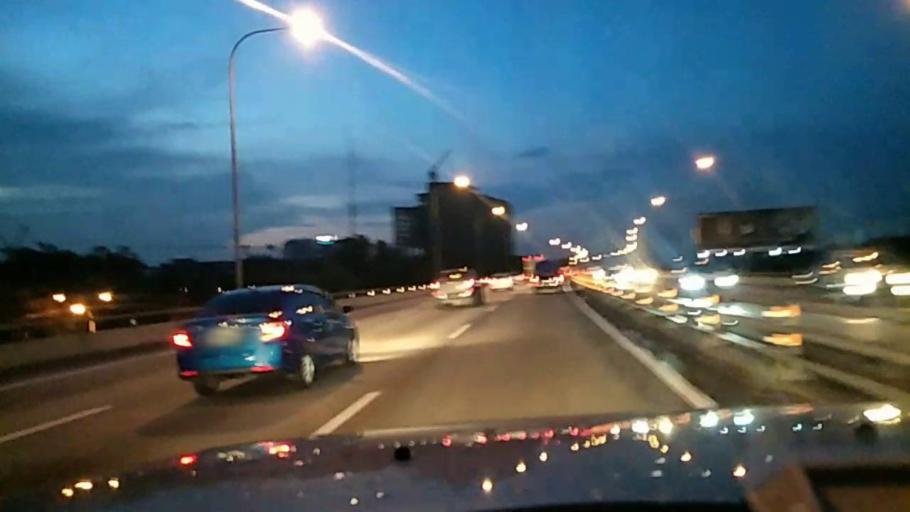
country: MY
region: Selangor
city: Shah Alam
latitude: 3.0799
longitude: 101.5516
